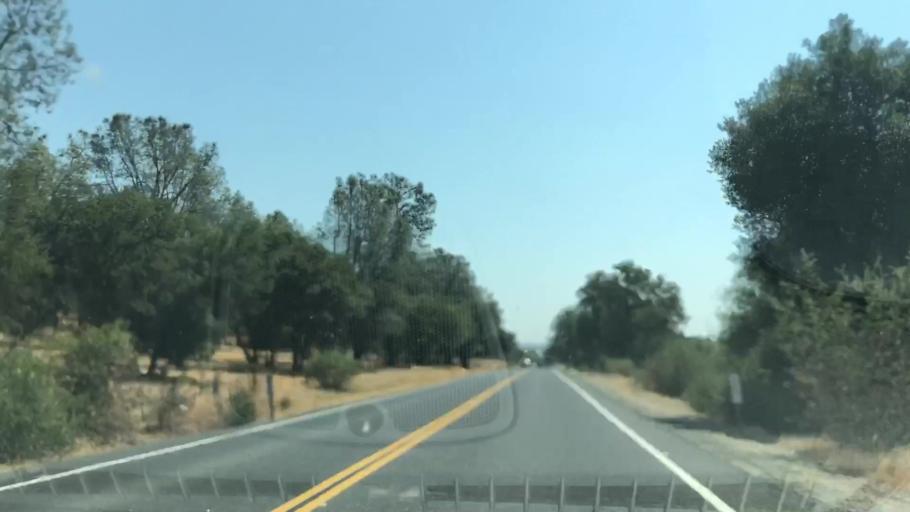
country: US
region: California
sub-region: Calaveras County
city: Copperopolis
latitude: 37.9461
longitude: -120.6089
